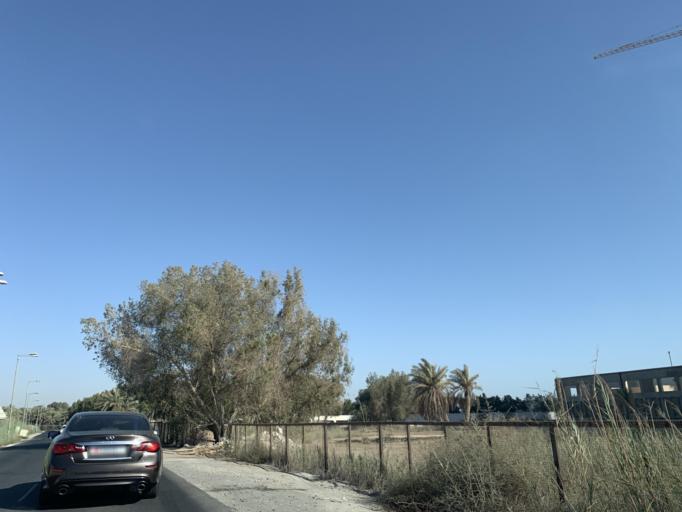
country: BH
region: Manama
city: Jidd Hafs
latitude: 26.2045
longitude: 50.4530
